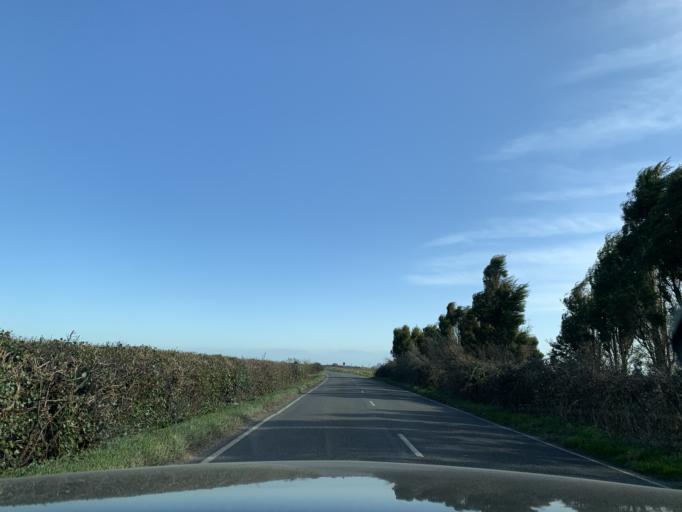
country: GB
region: England
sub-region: Kent
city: Lydd
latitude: 50.9494
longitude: 0.9166
